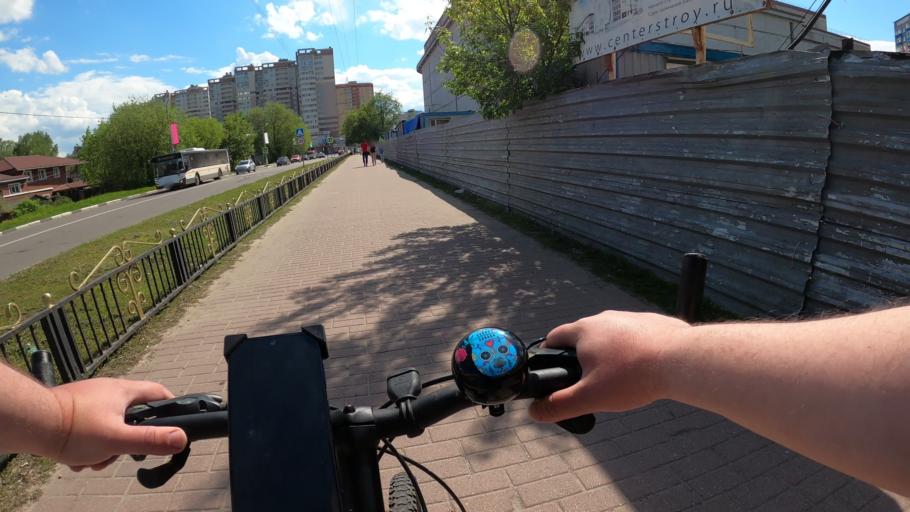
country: RU
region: Moskovskaya
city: Ramenskoye
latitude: 55.5794
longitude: 38.2077
